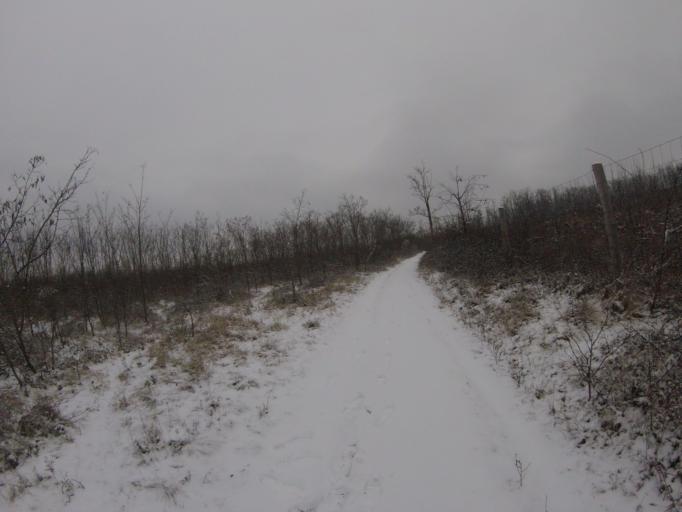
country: HU
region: Fejer
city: Pakozd
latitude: 47.2294
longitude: 18.5324
